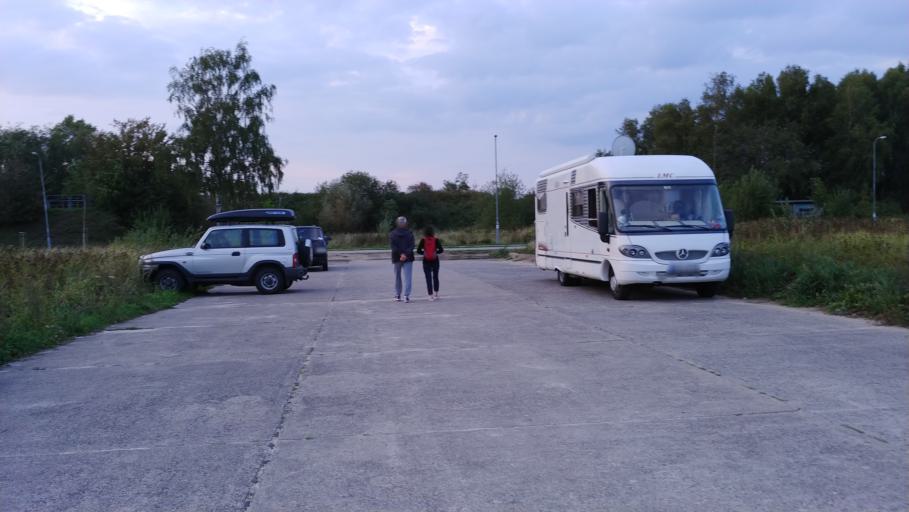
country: PL
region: West Pomeranian Voivodeship
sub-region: Powiat kolobrzeski
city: Kolobrzeg
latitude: 54.1977
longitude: 15.6633
